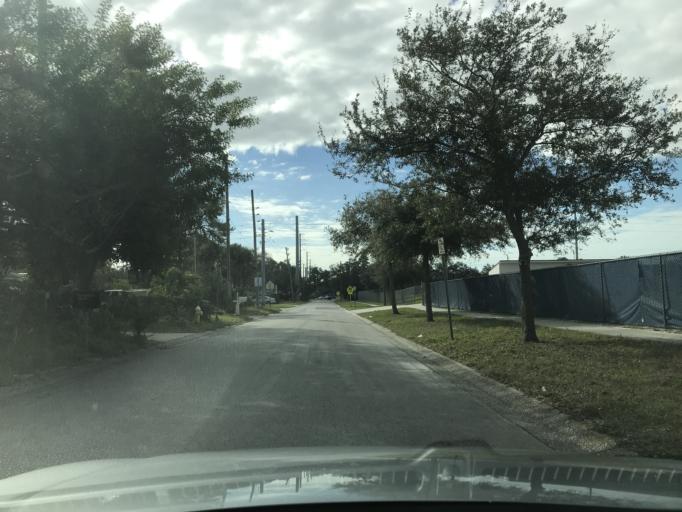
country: US
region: Florida
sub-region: Pinellas County
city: Largo
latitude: 27.9192
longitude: -82.7834
